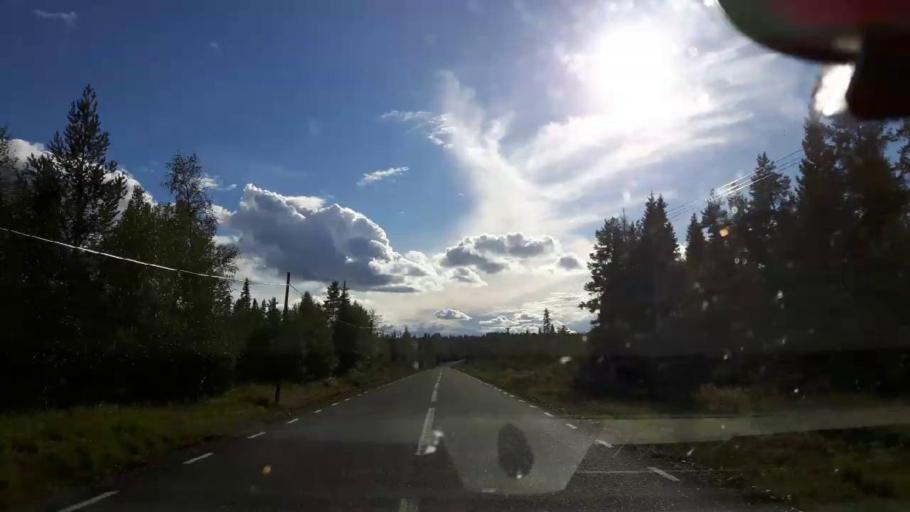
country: SE
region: Jaemtland
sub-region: Stroemsunds Kommun
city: Stroemsund
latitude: 63.5717
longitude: 15.6218
